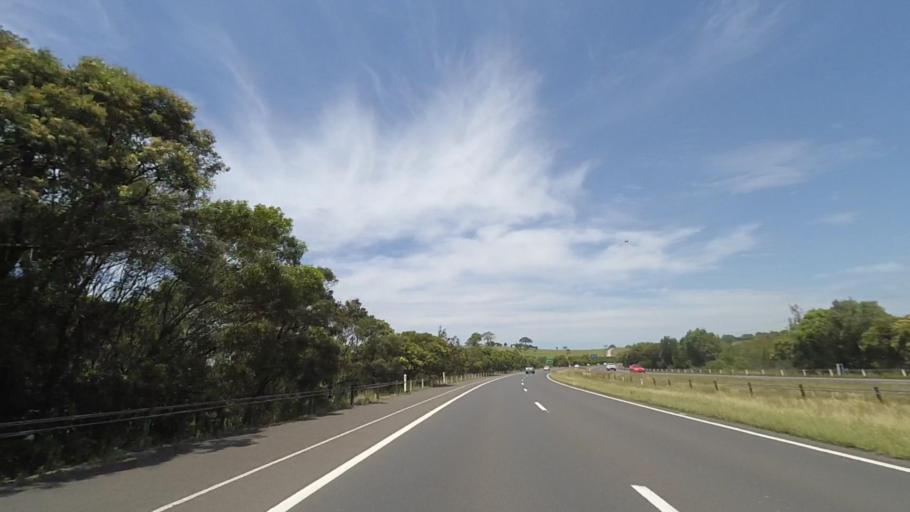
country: AU
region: New South Wales
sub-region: Shellharbour
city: Croom
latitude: -34.6166
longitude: 150.8381
